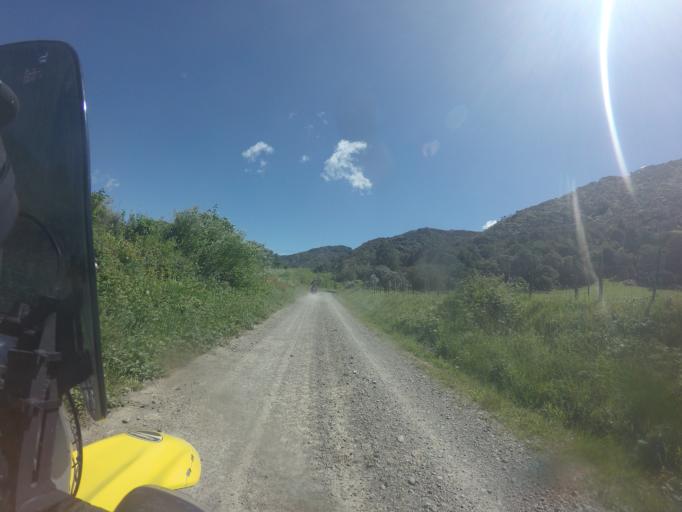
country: NZ
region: Bay of Plenty
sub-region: Opotiki District
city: Opotiki
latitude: -38.3020
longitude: 177.3330
